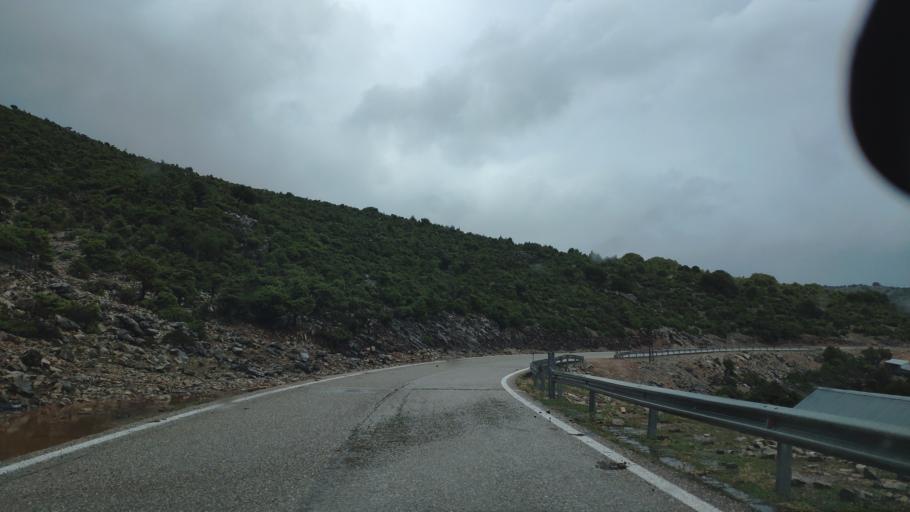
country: GR
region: West Greece
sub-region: Nomos Aitolias kai Akarnanias
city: Krikellos
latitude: 39.0706
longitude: 21.3842
